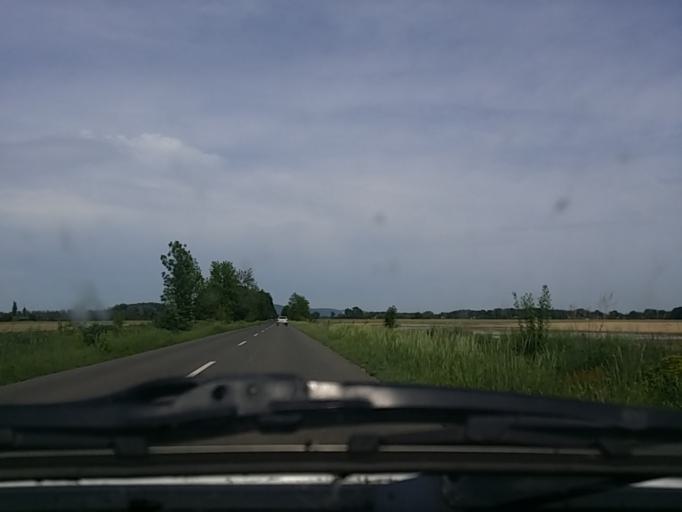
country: HR
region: Osjecko-Baranjska
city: Viljevo
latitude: 45.8316
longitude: 18.1186
